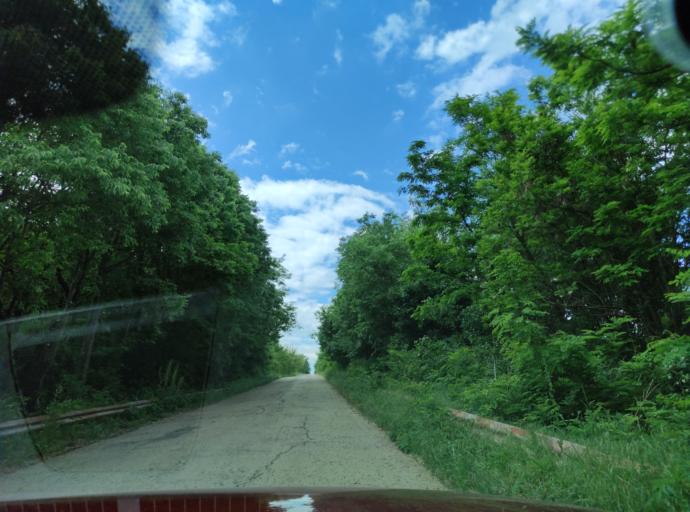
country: BG
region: Montana
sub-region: Obshtina Berkovitsa
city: Berkovitsa
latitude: 43.3561
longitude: 23.0949
